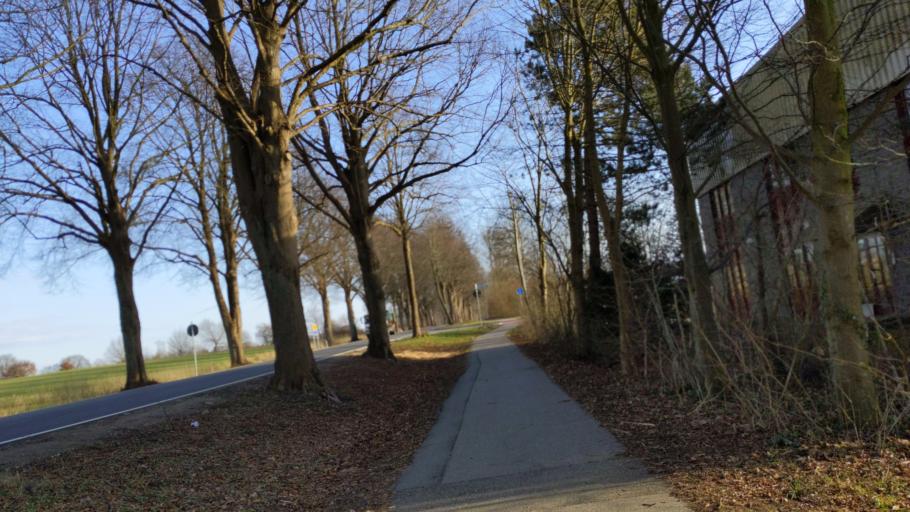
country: DE
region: Schleswig-Holstein
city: Ratekau
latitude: 53.9580
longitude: 10.7242
